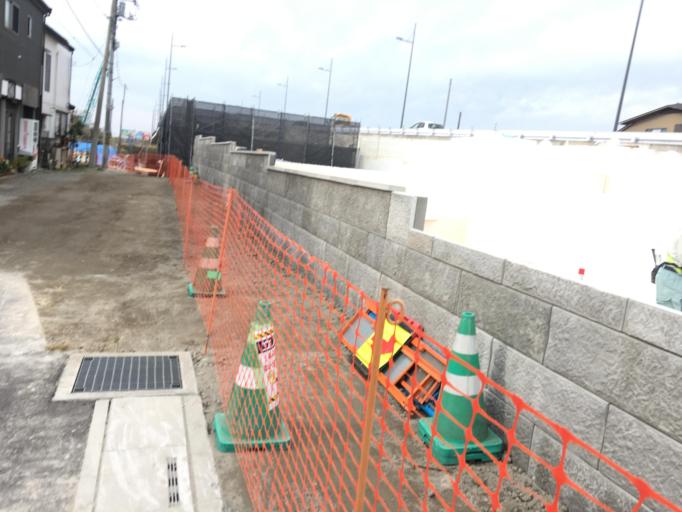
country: JP
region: Saitama
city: Yoshikawa
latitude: 35.8855
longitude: 139.8393
